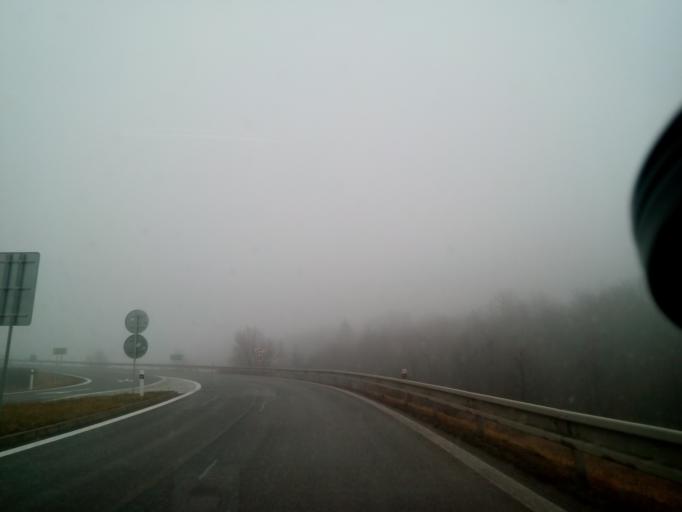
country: SK
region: Kosicky
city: Krompachy
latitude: 49.0083
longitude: 20.9428
